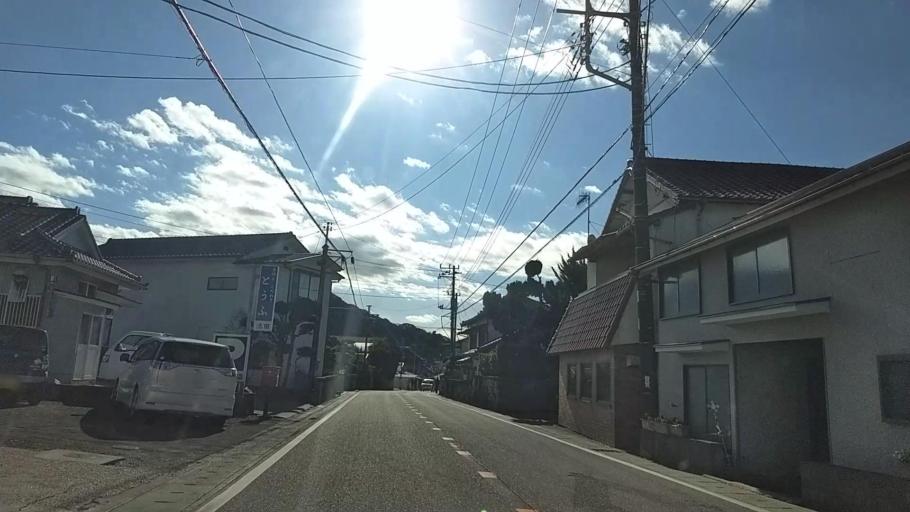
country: JP
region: Chiba
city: Tateyama
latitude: 35.0612
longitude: 139.8273
